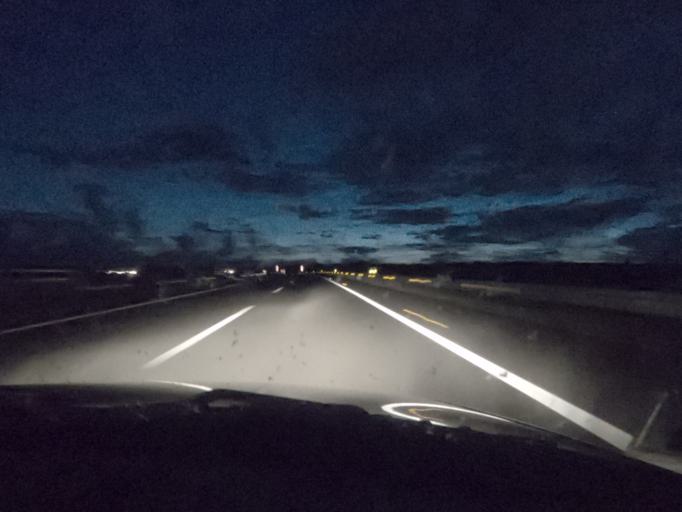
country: ES
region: Extremadura
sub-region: Provincia de Caceres
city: Coria
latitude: 39.9887
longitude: -6.4678
